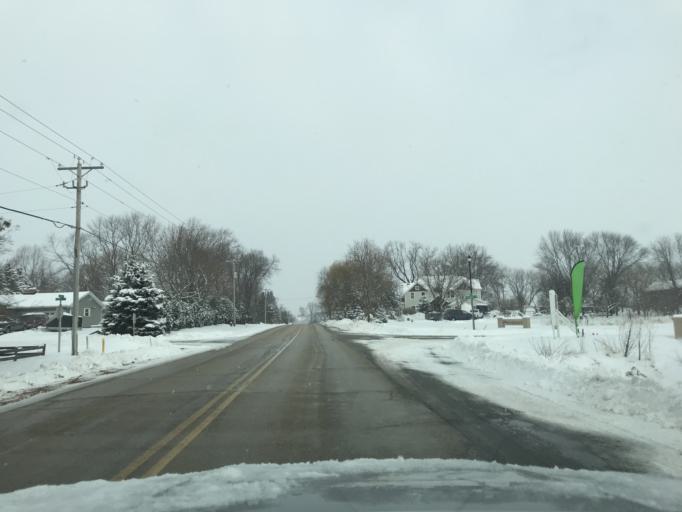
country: US
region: Wisconsin
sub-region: Dane County
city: Sun Prairie
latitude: 43.1674
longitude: -89.2852
